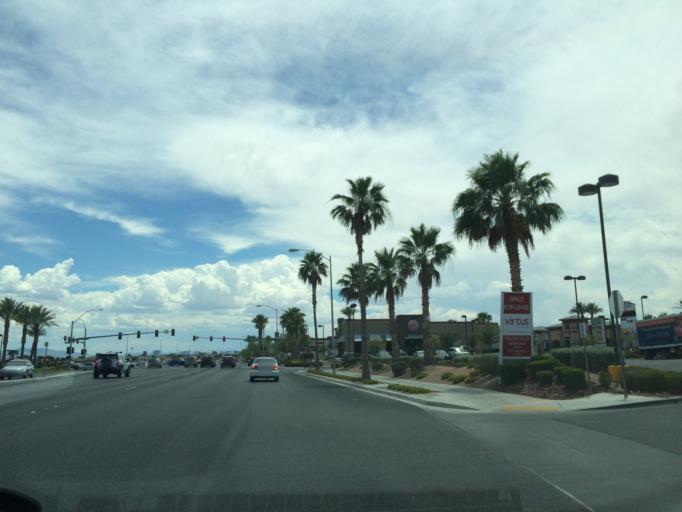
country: US
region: Nevada
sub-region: Clark County
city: North Las Vegas
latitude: 36.2630
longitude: -115.1801
